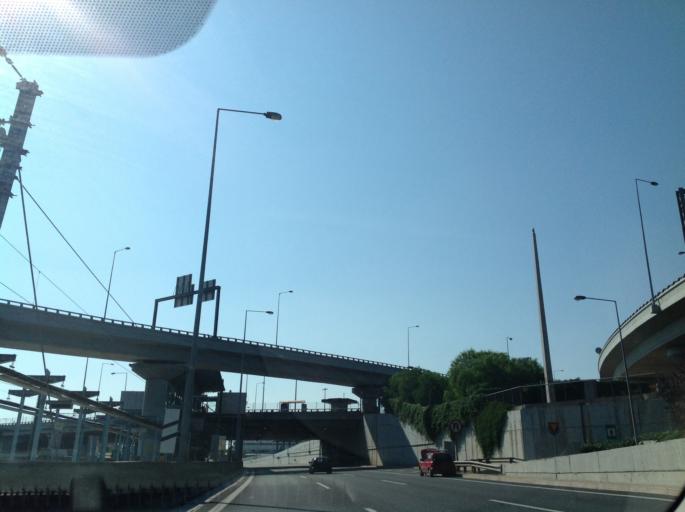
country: GR
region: Attica
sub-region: Nomarchia Athinas
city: Agia Paraskevi
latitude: 38.0253
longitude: 23.8322
